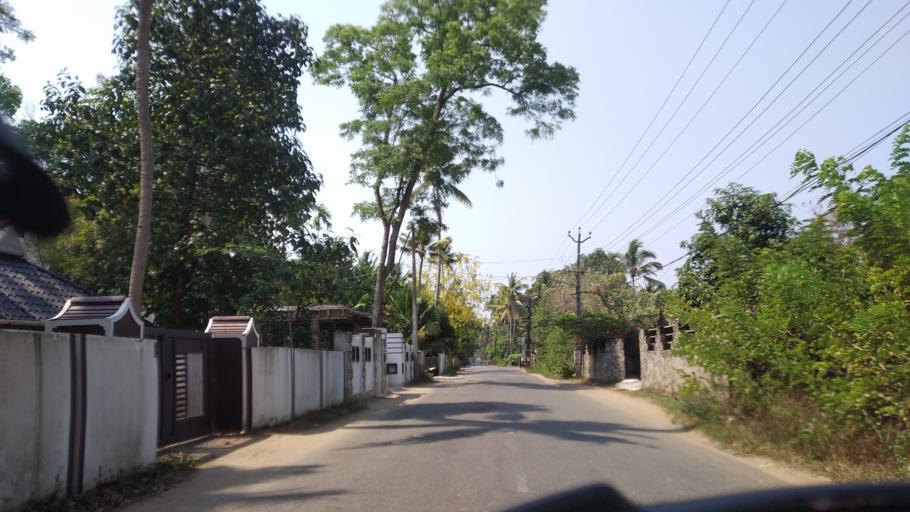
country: IN
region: Kerala
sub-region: Thrissur District
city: Kodungallur
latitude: 10.2508
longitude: 76.1482
